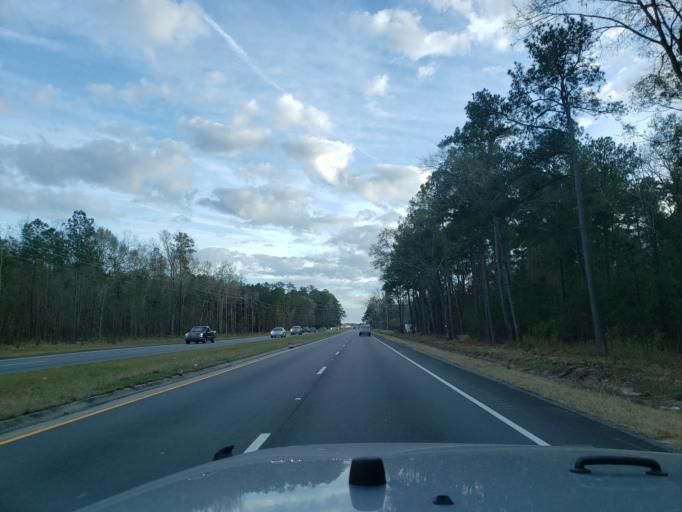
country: US
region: Georgia
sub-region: Chatham County
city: Port Wentworth
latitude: 32.2060
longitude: -81.2005
